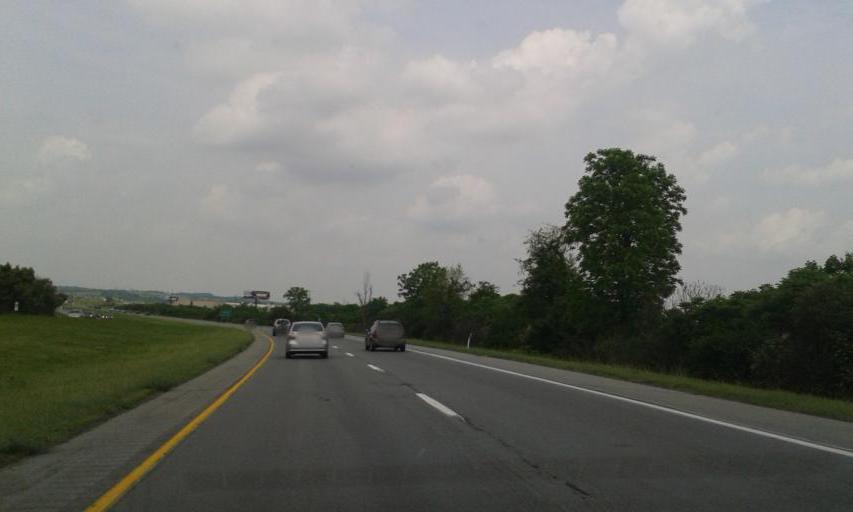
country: US
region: Pennsylvania
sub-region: Northampton County
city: Tatamy
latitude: 40.7279
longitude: -75.2745
